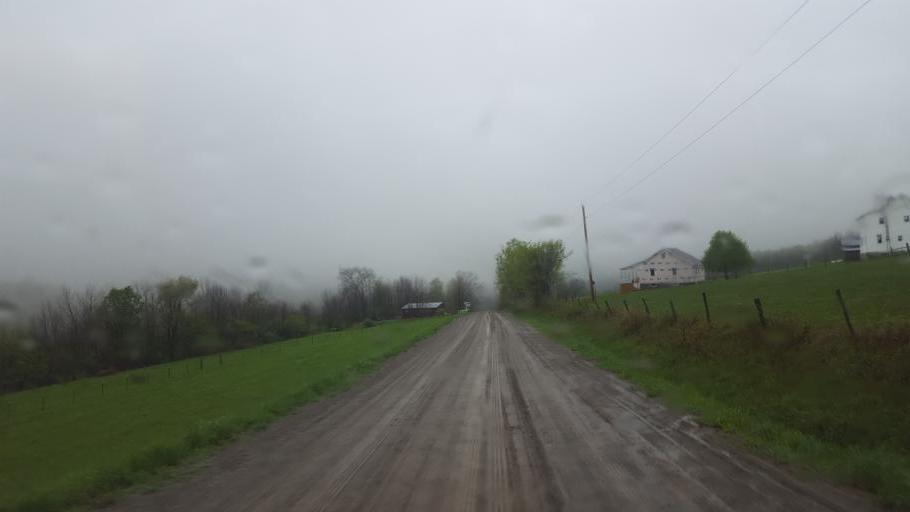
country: US
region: Pennsylvania
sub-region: Tioga County
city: Elkland
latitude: 42.0603
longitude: -77.4325
